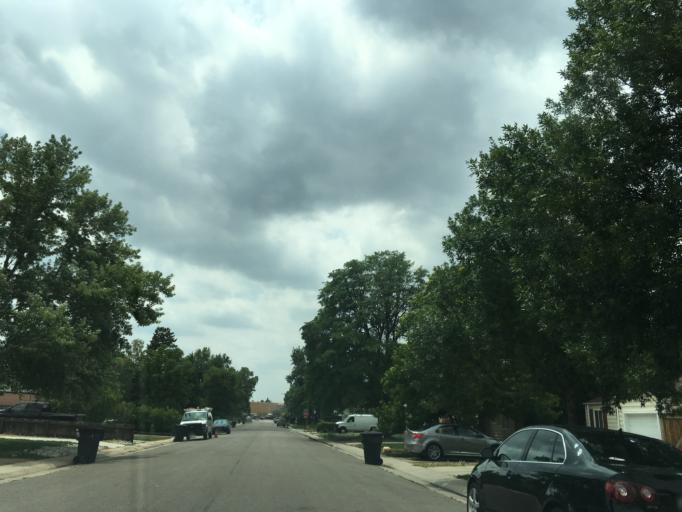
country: US
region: Colorado
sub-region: Arapahoe County
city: Sheridan
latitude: 39.6812
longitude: -105.0276
